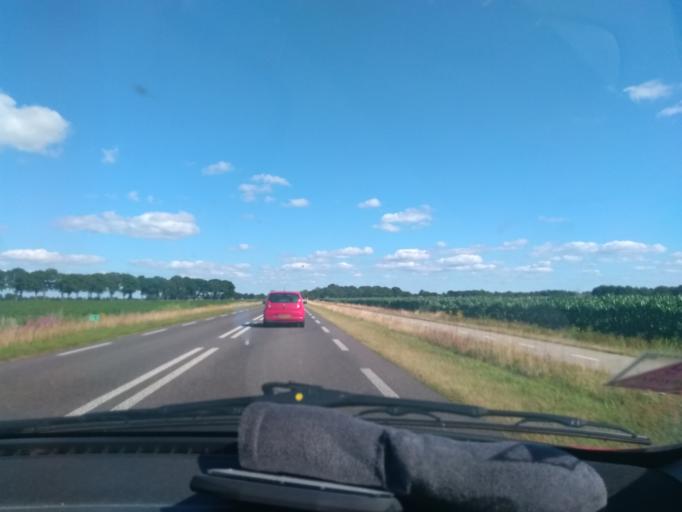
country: NL
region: Drenthe
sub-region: Gemeente Tynaarlo
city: Vries
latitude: 53.1039
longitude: 6.5350
